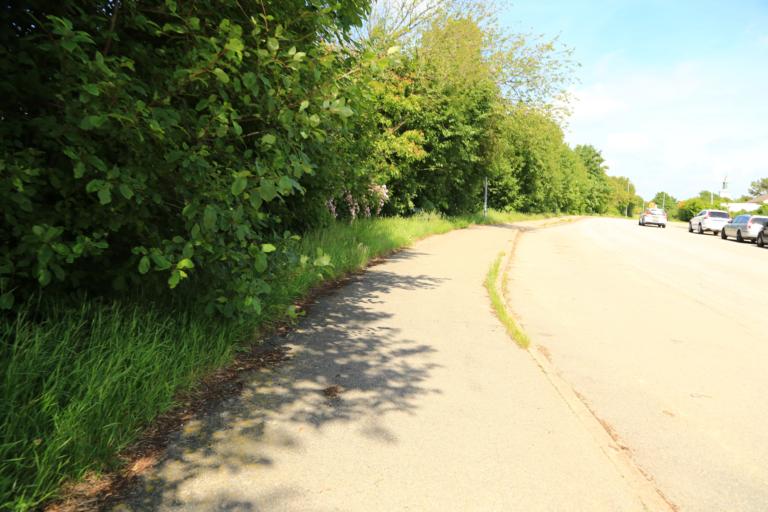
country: SE
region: Halland
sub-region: Varbergs Kommun
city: Varberg
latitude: 57.1057
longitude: 12.2915
